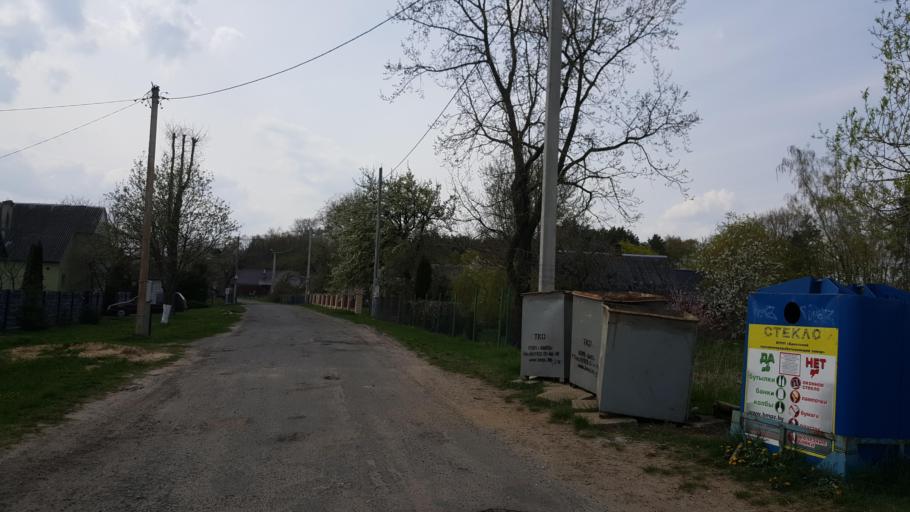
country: BY
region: Brest
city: Zhabinka
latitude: 52.2199
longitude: 23.9251
